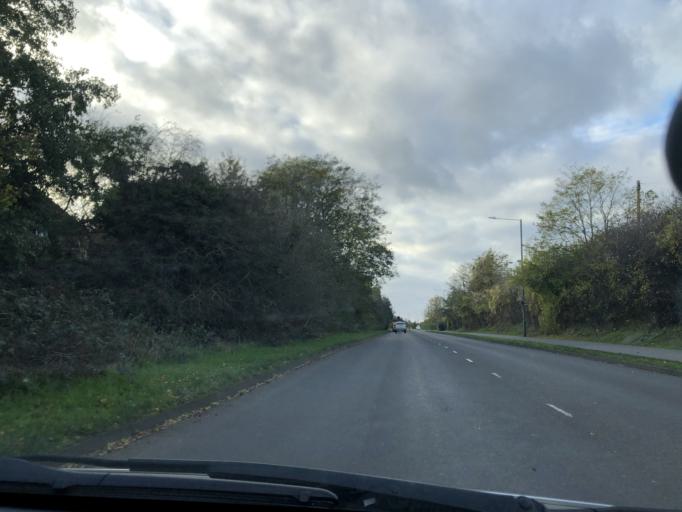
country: GB
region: England
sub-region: Kent
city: Dartford
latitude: 51.4381
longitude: 0.2112
